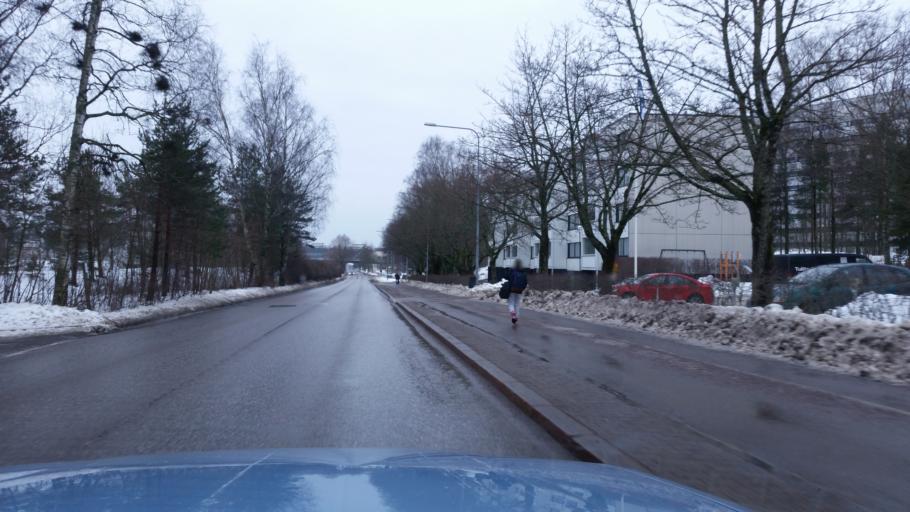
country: FI
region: Uusimaa
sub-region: Helsinki
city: Vantaa
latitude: 60.2354
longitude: 25.0800
